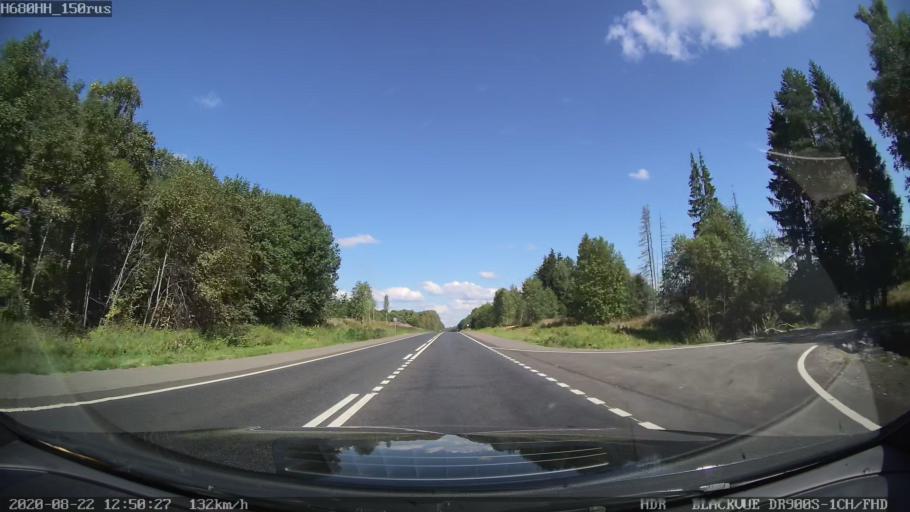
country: RU
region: Tverskaya
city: Rameshki
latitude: 57.4669
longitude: 36.2243
